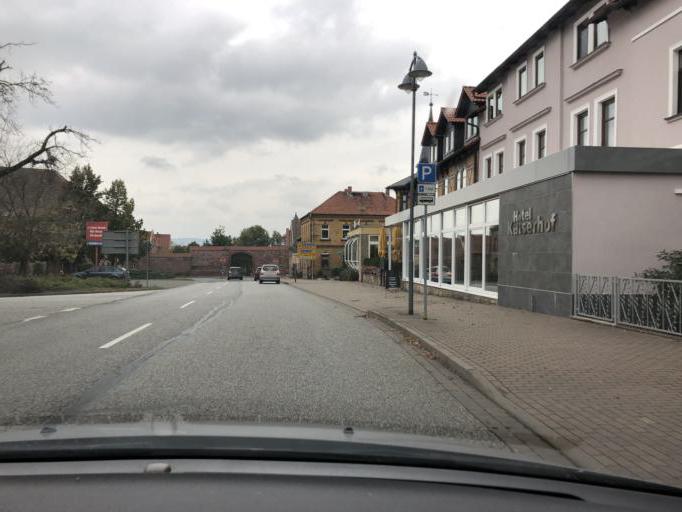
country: DE
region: Saxony-Anhalt
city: Kelbra
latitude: 51.4348
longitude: 11.0435
